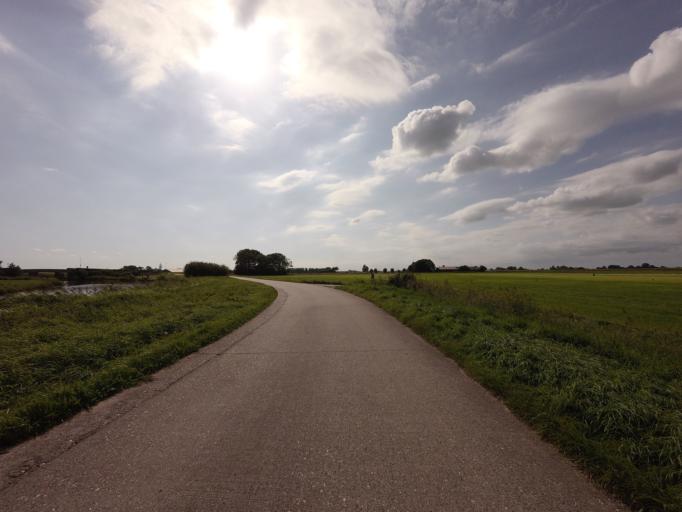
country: NL
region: Friesland
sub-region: Sudwest Fryslan
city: Scharnegoutum
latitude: 53.0777
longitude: 5.6316
